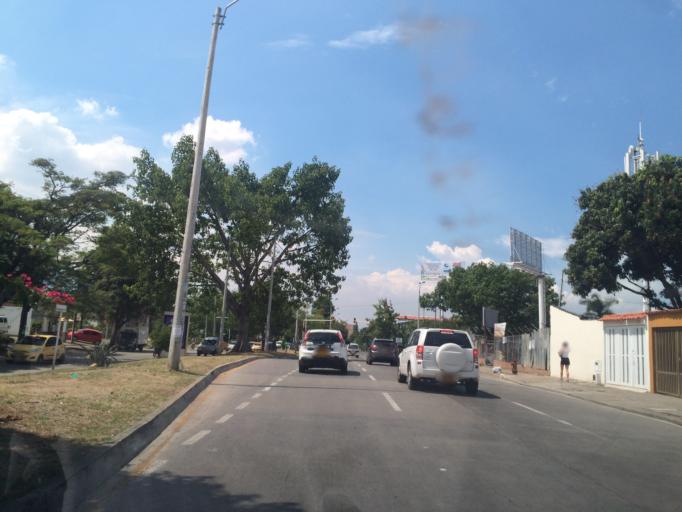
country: CO
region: Valle del Cauca
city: Cali
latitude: 3.4014
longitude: -76.5275
